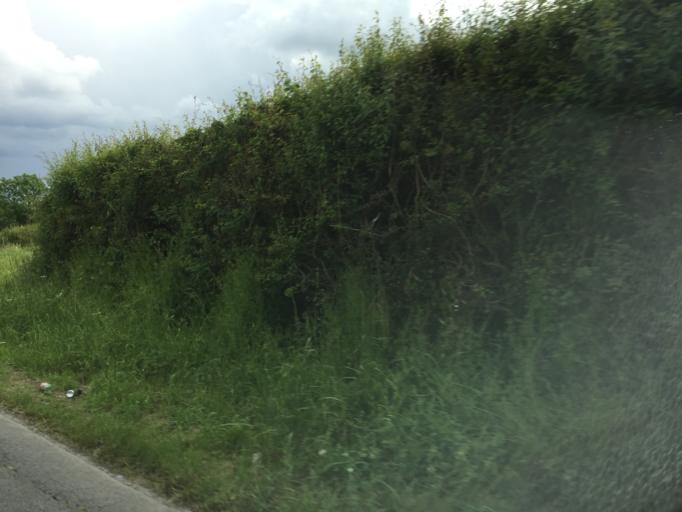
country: GB
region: England
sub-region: Wiltshire
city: Cricklade
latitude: 51.6242
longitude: -1.8566
